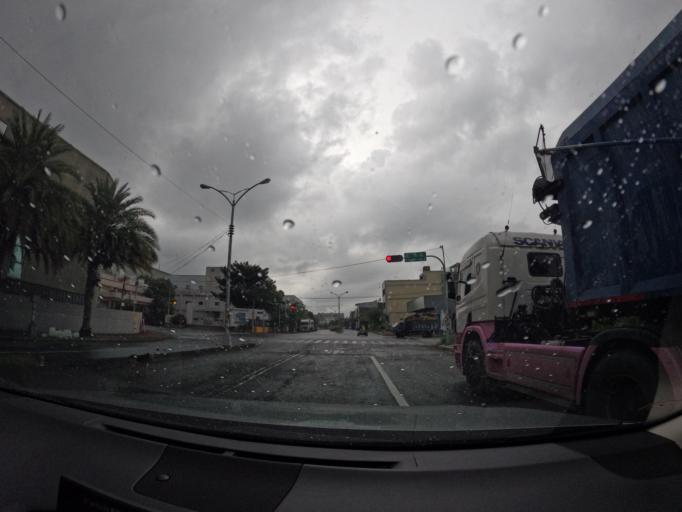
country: TW
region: Taiwan
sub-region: Nantou
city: Nantou
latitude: 23.9208
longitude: 120.6649
